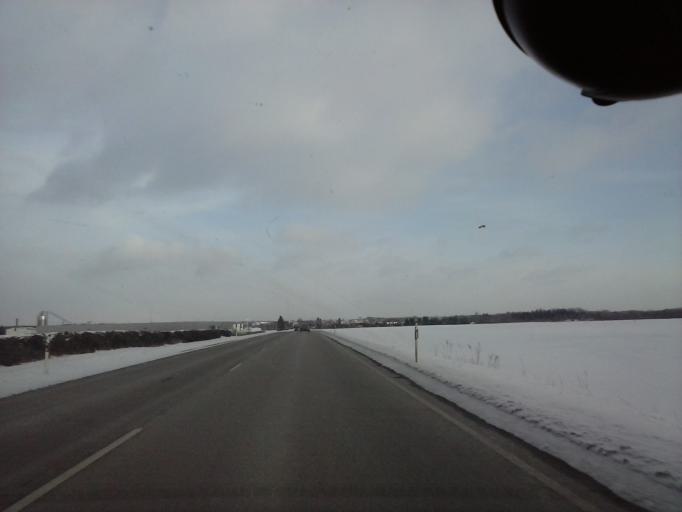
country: EE
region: Tartu
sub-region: Noo vald
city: Noo
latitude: 58.3546
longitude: 26.5837
